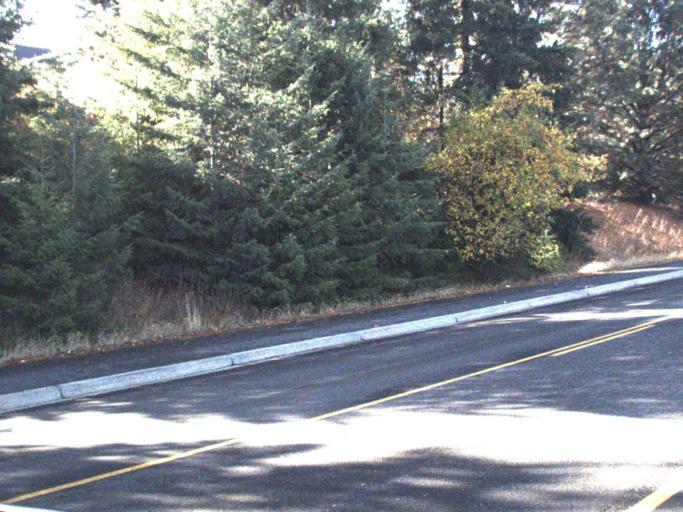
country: US
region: Washington
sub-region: Whitman County
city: Pullman
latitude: 46.7337
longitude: -117.1966
